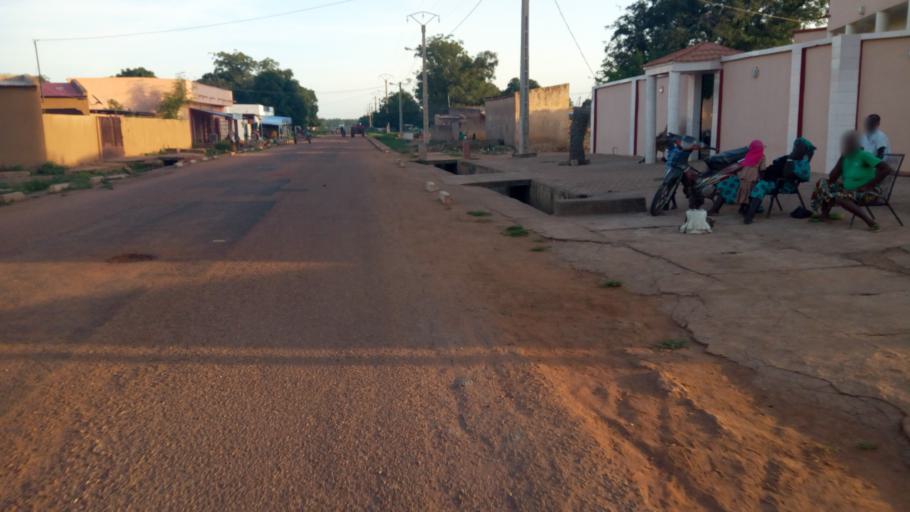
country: ML
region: Sikasso
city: Koutiala
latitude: 12.4072
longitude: -5.4450
